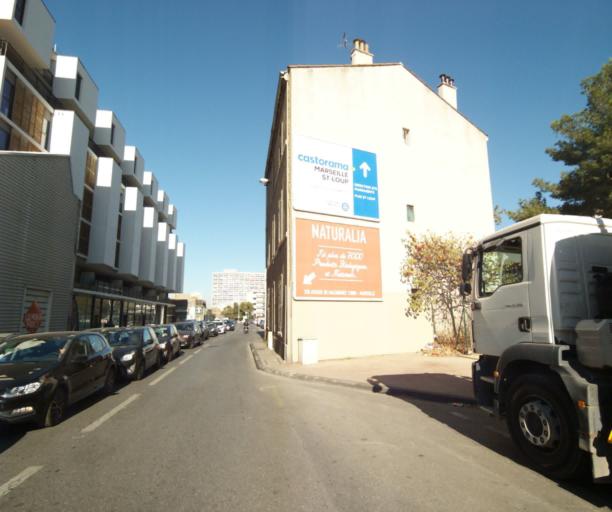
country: FR
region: Provence-Alpes-Cote d'Azur
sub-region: Departement des Bouches-du-Rhone
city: Marseille 09
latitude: 43.2595
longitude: 5.3941
